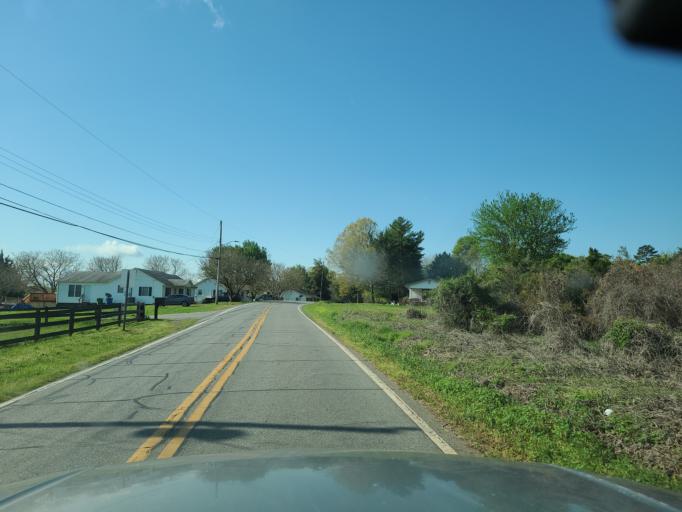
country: US
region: North Carolina
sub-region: Rutherford County
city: Spindale
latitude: 35.3767
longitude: -81.9230
